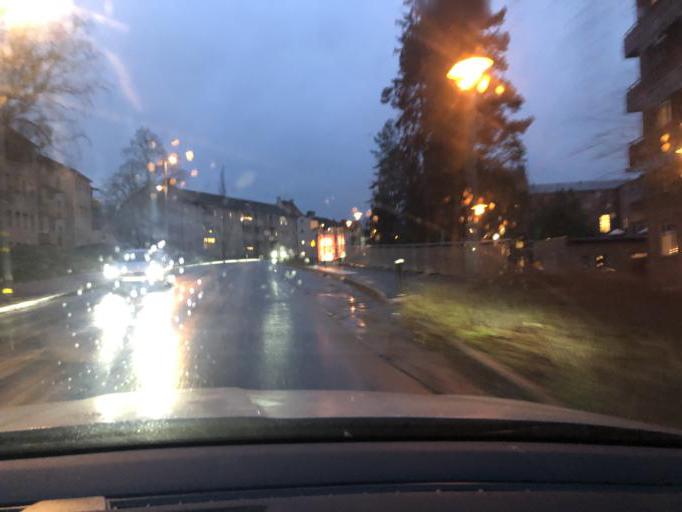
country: SE
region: Vaermland
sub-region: Karlstads Kommun
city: Karlstad
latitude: 59.3758
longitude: 13.4822
